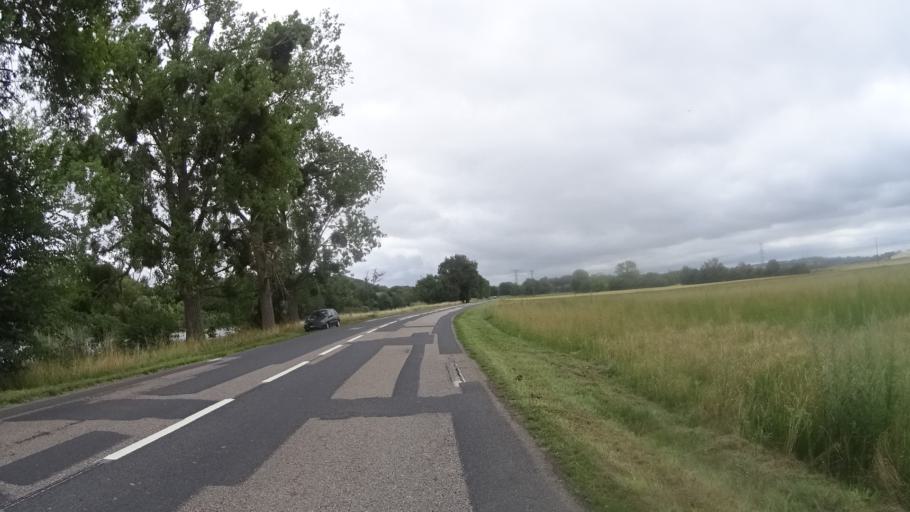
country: FR
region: Lorraine
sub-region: Departement de Meurthe-et-Moselle
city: Laneuveville-devant-Nancy
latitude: 48.6603
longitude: 6.2391
